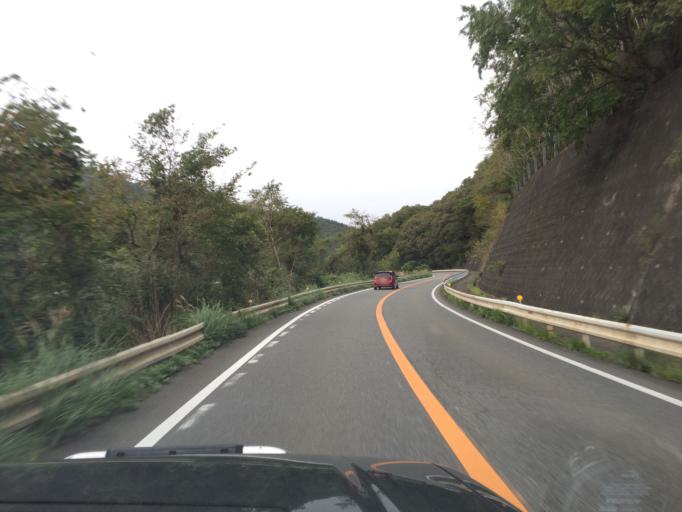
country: JP
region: Hyogo
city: Toyooka
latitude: 35.3703
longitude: 134.8176
